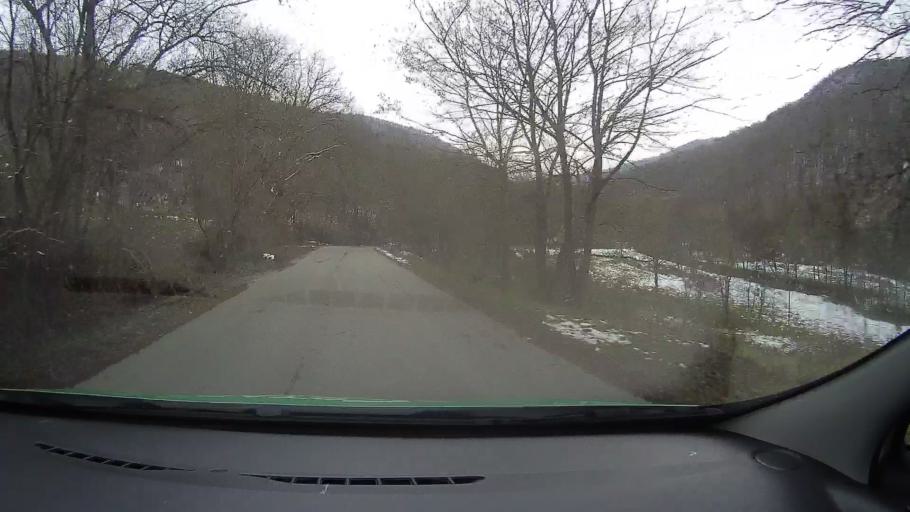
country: RO
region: Hunedoara
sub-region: Comuna Balsa
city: Balsa
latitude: 46.0150
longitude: 23.1494
